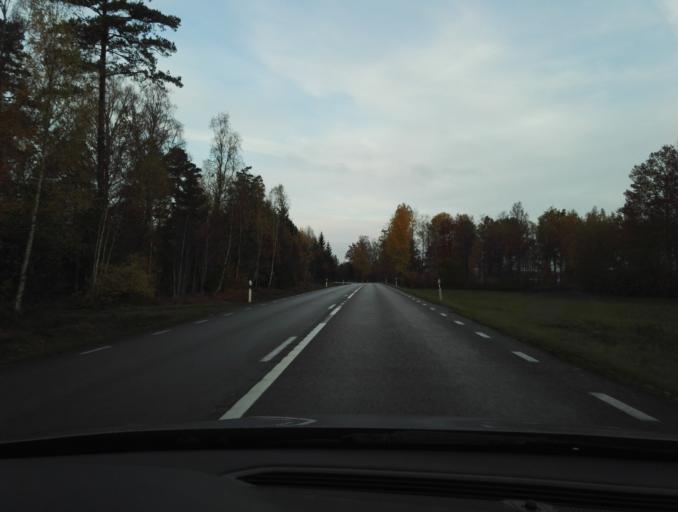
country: SE
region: Kronoberg
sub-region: Vaxjo Kommun
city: Gemla
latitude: 56.9686
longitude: 14.7116
